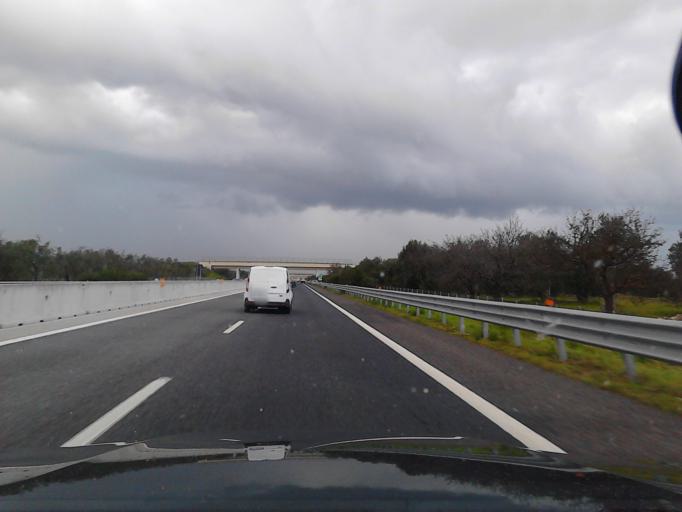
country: IT
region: Apulia
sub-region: Provincia di Bari
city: Bitonto
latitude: 41.1144
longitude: 16.7346
